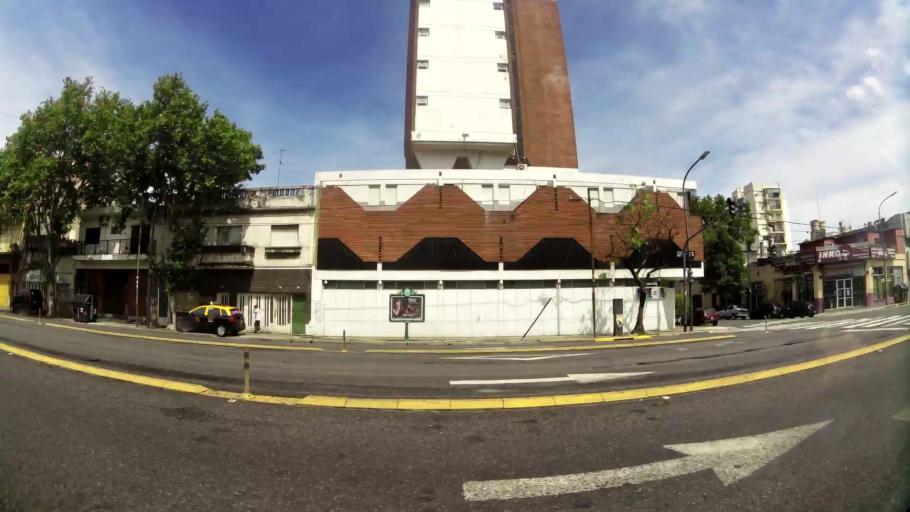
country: AR
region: Buenos Aires F.D.
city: Villa Santa Rita
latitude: -34.6232
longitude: -58.4816
